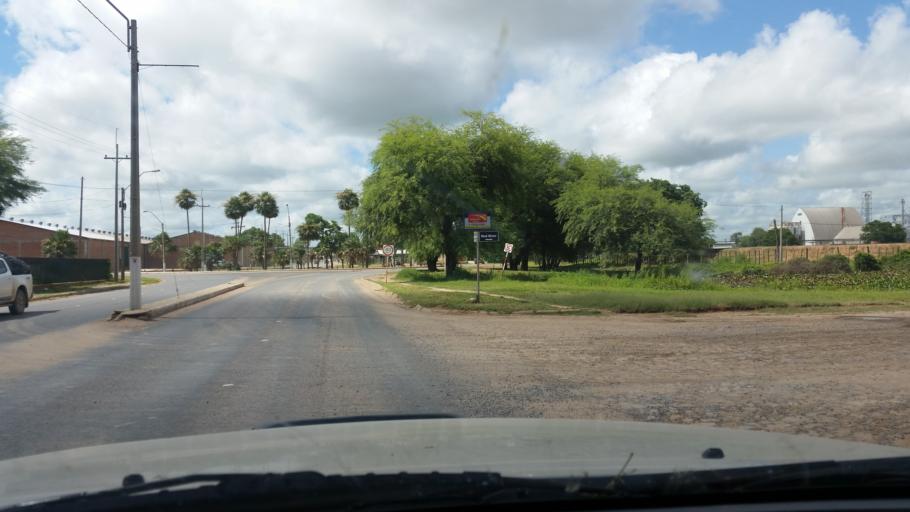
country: PY
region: Boqueron
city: Colonia Menno
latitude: -22.3766
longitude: -59.8371
